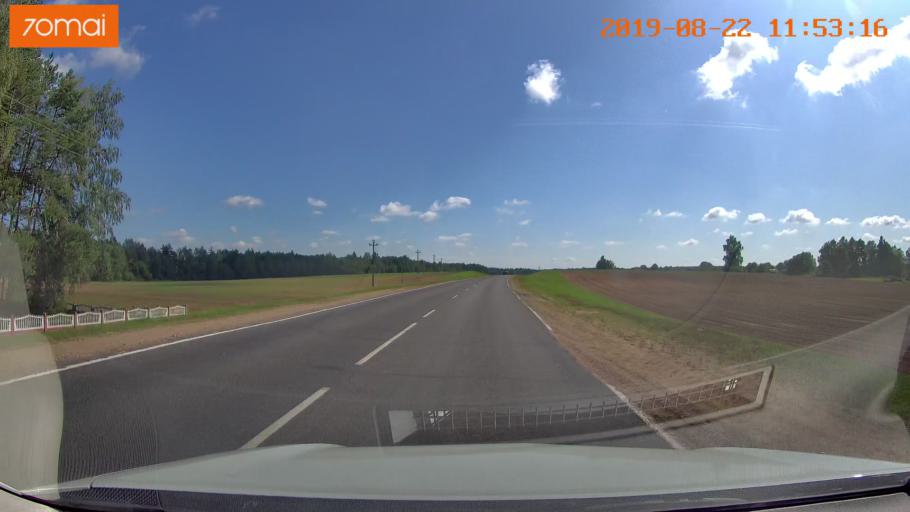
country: BY
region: Minsk
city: Uzda
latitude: 53.4378
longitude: 27.4991
